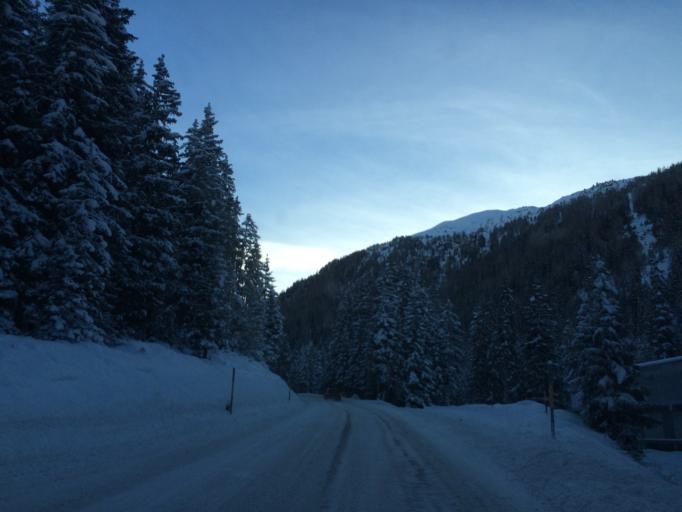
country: CH
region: Grisons
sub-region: Praettigau/Davos District
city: Davos
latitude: 46.8089
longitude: 9.8638
